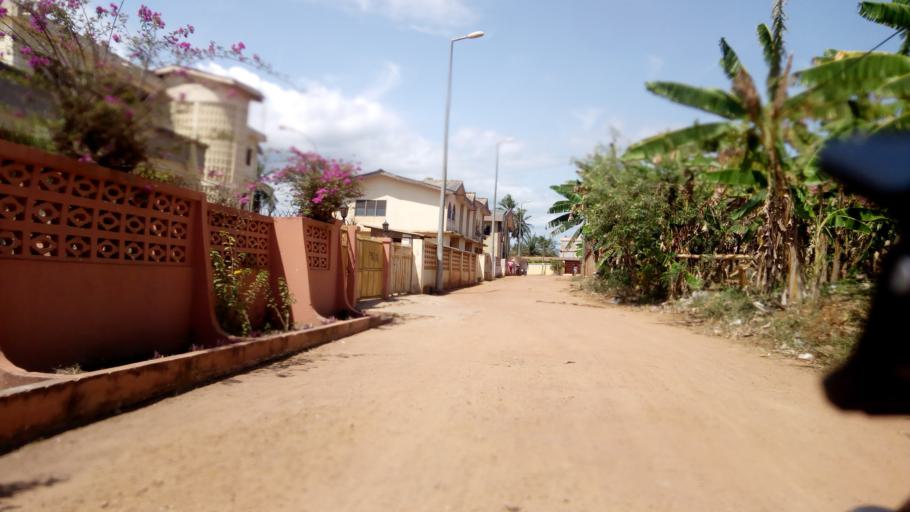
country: GH
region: Central
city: Cape Coast
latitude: 5.1327
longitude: -1.2800
